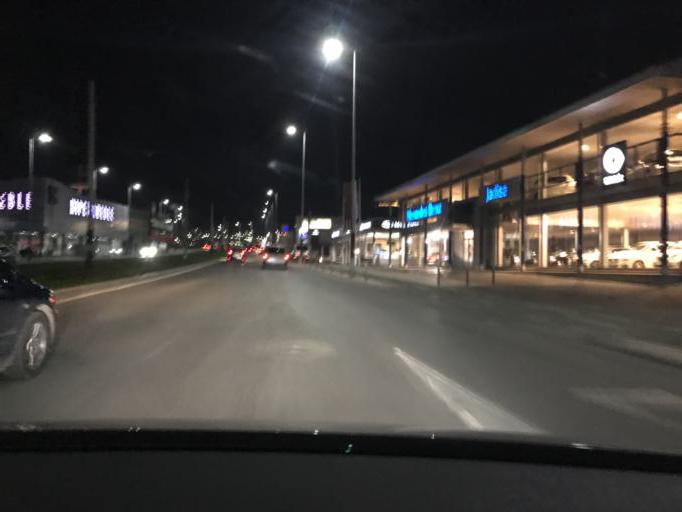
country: ES
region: Andalusia
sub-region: Provincia de Jaen
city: Jaen
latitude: 37.7946
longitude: -3.7801
